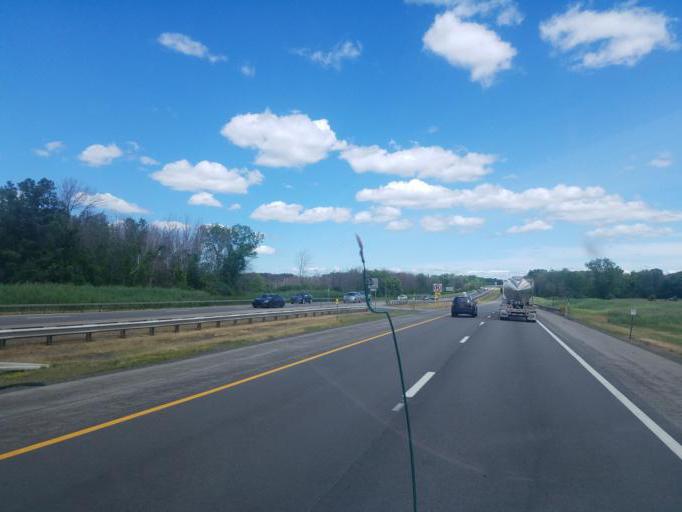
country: US
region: New York
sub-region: Monroe County
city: Scottsville
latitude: 43.0479
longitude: -77.6450
